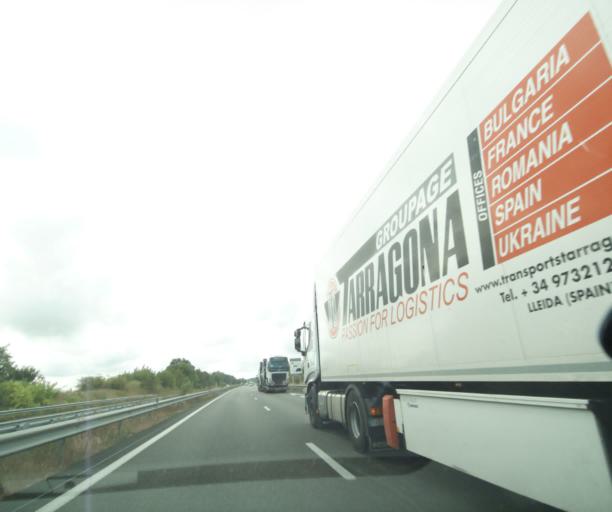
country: FR
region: Poitou-Charentes
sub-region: Departement de la Charente-Maritime
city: Saint-Genis-de-Saintonge
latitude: 45.4358
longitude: -0.6059
